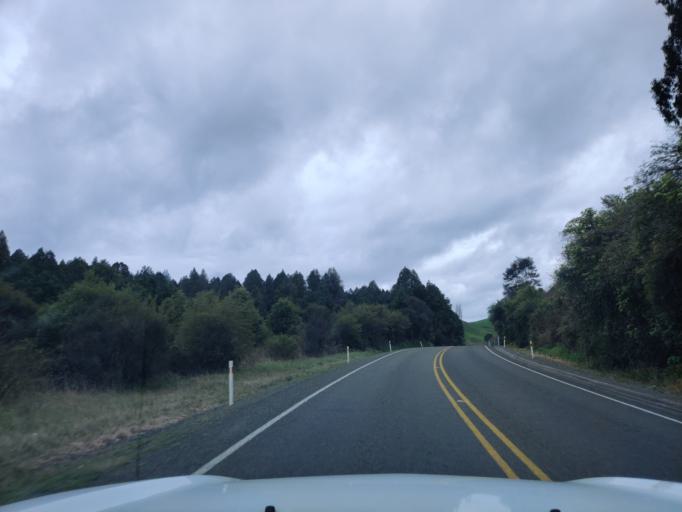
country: NZ
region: Waikato
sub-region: Otorohanga District
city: Otorohanga
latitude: -38.5281
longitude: 175.1755
